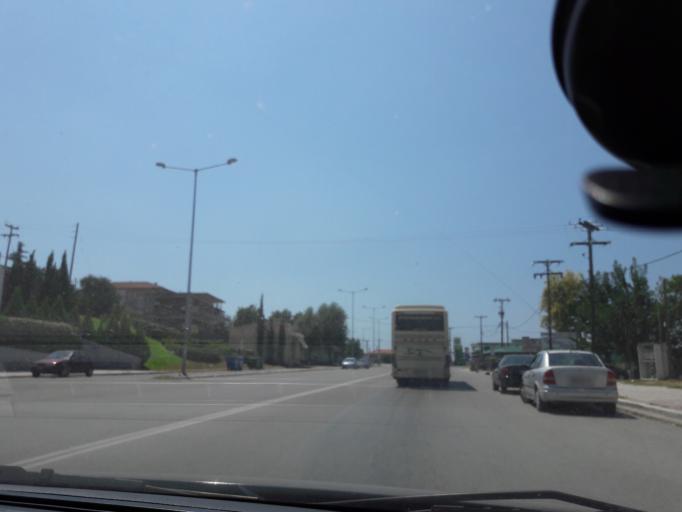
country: GR
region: Central Macedonia
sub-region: Nomos Chalkidikis
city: Nea Kallikrateia
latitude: 40.3198
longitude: 23.0656
